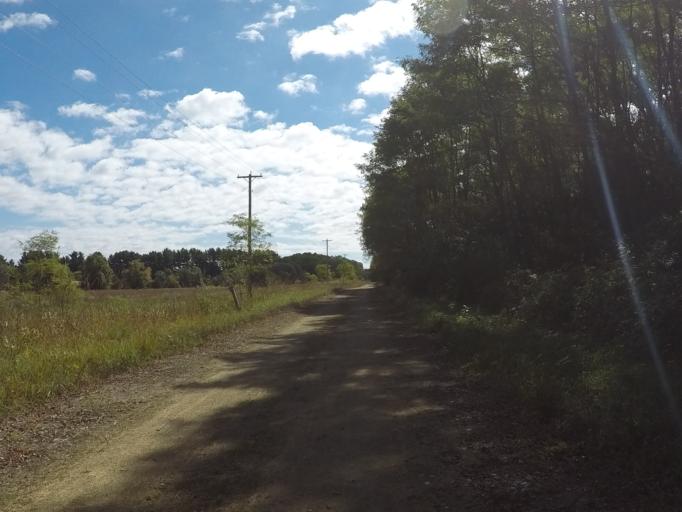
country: US
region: Wisconsin
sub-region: Sauk County
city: Spring Green
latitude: 43.1856
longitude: -90.2119
